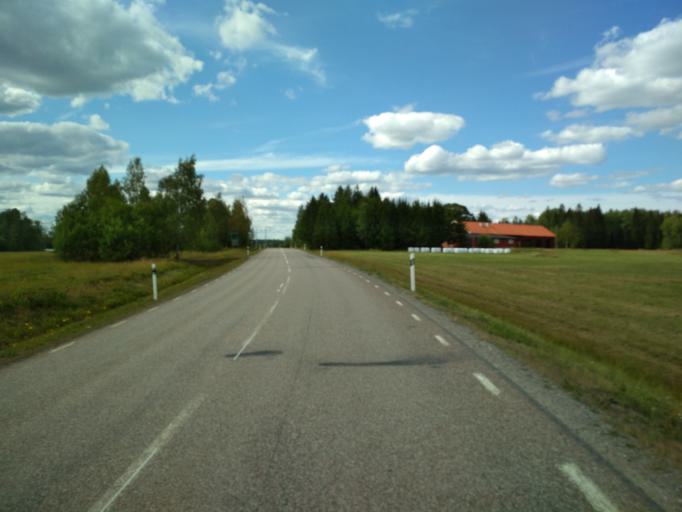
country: SE
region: Vaestmanland
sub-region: Sala Kommun
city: Sala
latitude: 59.9149
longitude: 16.5176
